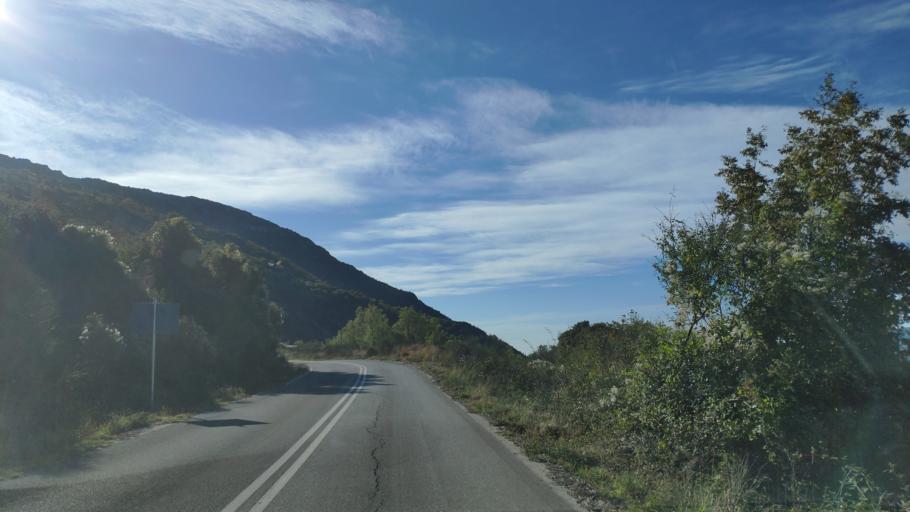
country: GR
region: Peloponnese
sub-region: Nomos Arkadias
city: Dimitsana
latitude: 37.5668
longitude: 22.0605
